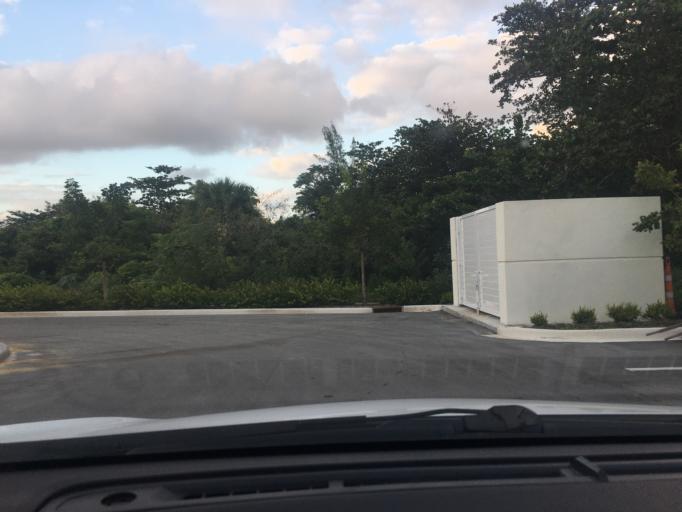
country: US
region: Florida
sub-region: Broward County
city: Dania Beach
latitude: 26.0744
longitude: -80.1739
